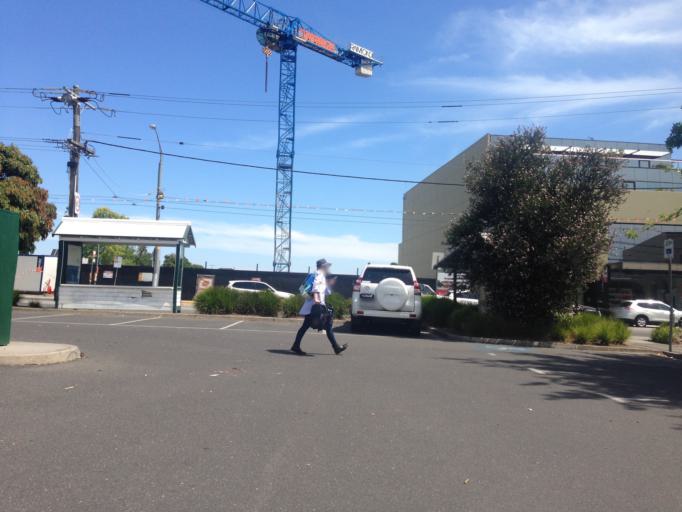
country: AU
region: Victoria
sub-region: Boroondara
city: Kew East
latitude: -37.7926
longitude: 145.0723
